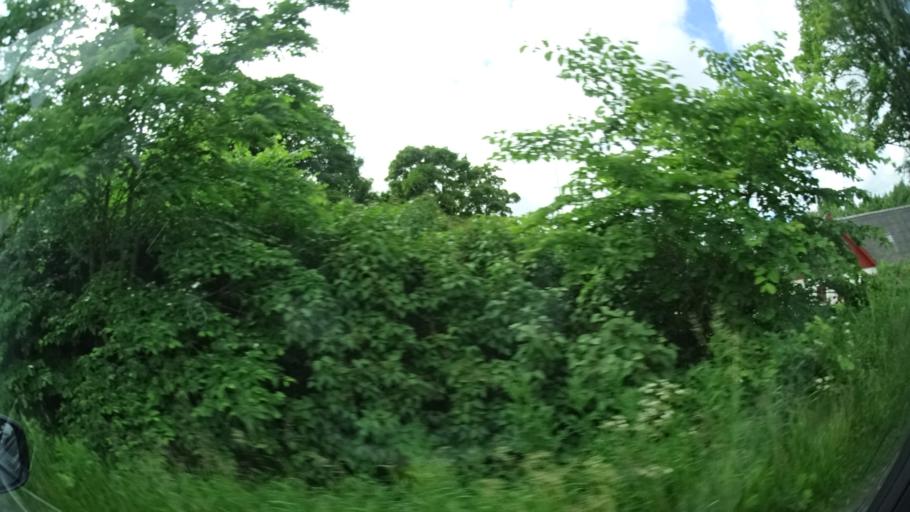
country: DK
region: Central Jutland
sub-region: Syddjurs Kommune
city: Ryomgard
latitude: 56.4267
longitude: 10.6109
